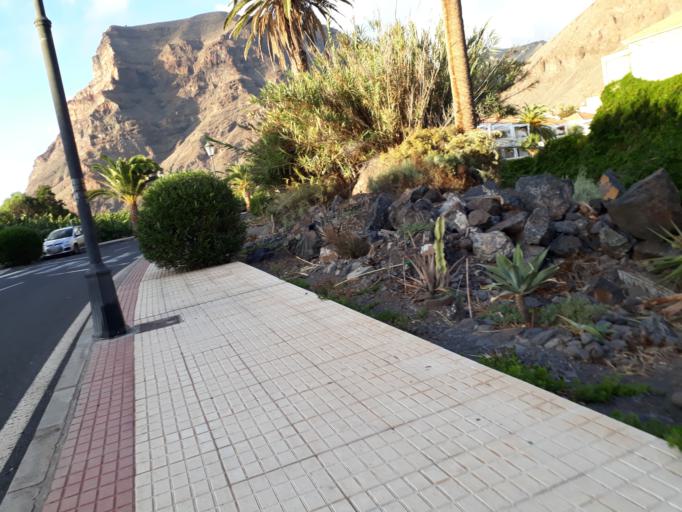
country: ES
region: Canary Islands
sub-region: Provincia de Santa Cruz de Tenerife
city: Alajero
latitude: 28.0871
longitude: -17.3364
